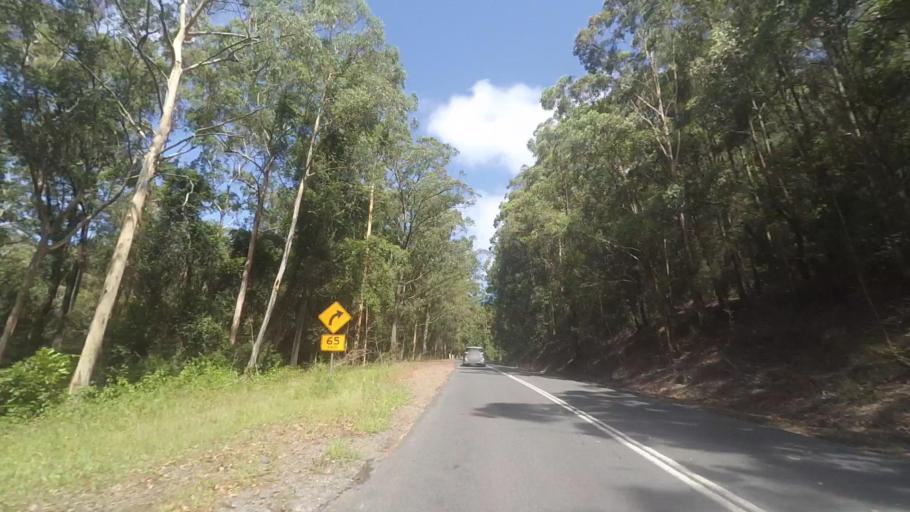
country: AU
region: New South Wales
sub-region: Great Lakes
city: Bulahdelah
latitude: -32.4033
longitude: 152.2963
